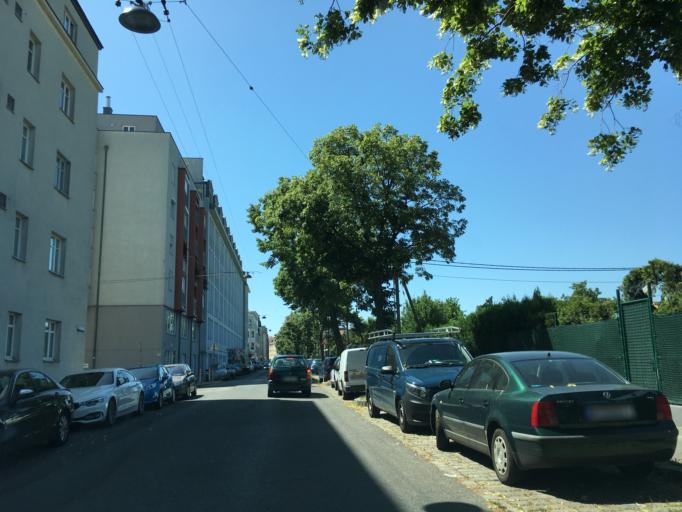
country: AT
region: Vienna
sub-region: Wien Stadt
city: Vienna
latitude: 48.2038
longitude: 16.3256
